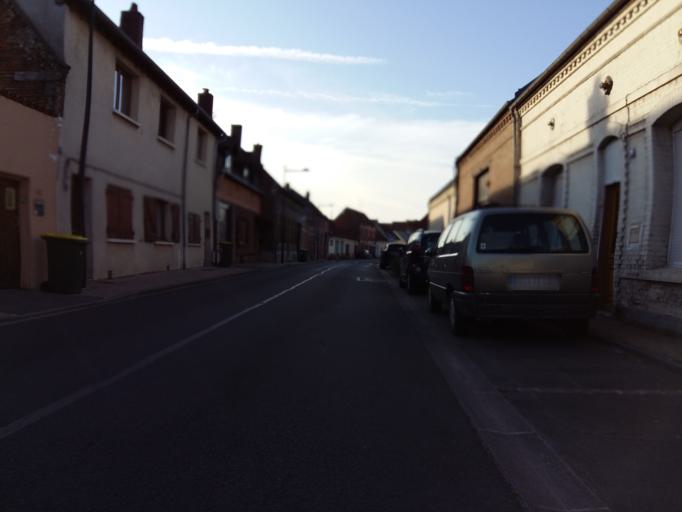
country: FR
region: Picardie
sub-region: Departement de la Somme
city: Camon
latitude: 49.8894
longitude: 2.3416
